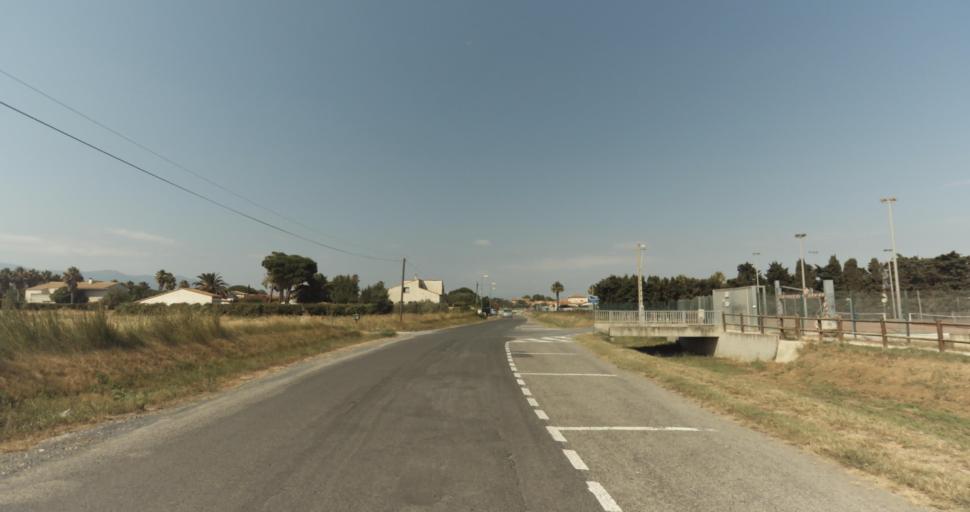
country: FR
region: Languedoc-Roussillon
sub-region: Departement des Pyrenees-Orientales
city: Latour-Bas-Elne
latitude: 42.6090
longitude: 3.0081
